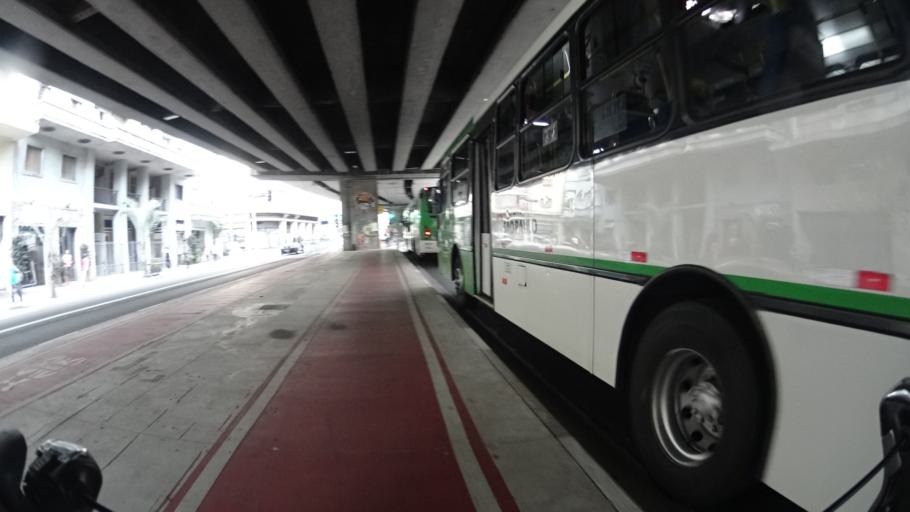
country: BR
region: Sao Paulo
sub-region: Sao Paulo
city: Sao Paulo
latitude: -23.5306
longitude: -46.6627
